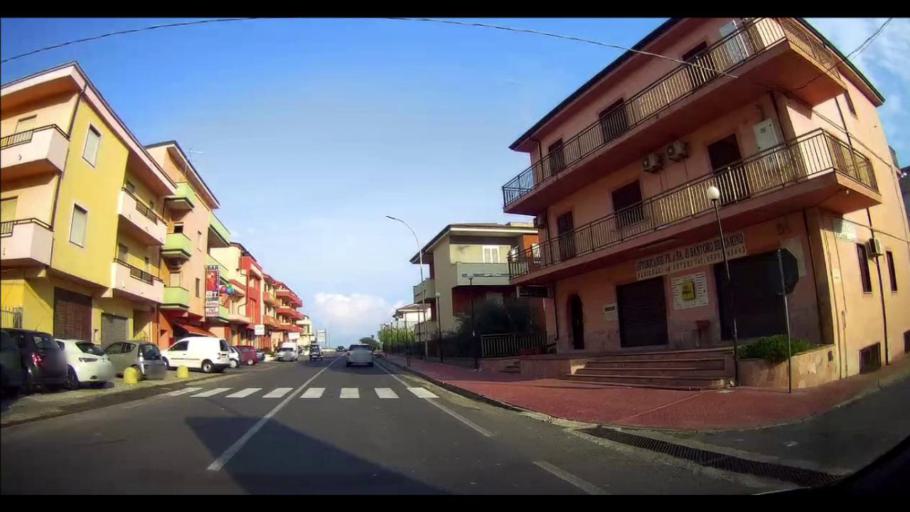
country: IT
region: Calabria
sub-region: Provincia di Cosenza
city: Cariati
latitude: 39.5058
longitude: 16.9371
